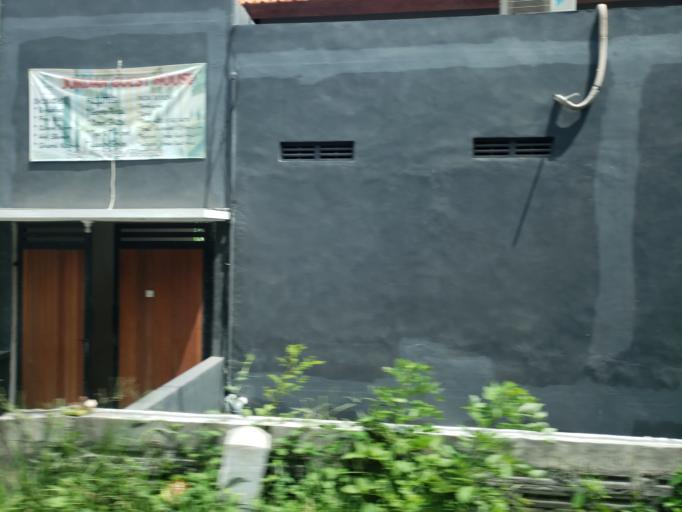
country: ID
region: Bali
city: Kangin
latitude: -8.8245
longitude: 115.1454
